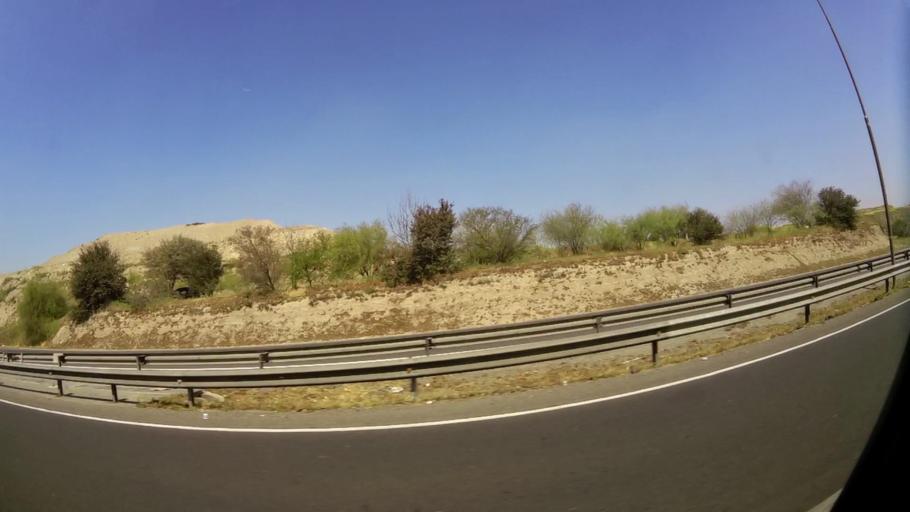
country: CL
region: Santiago Metropolitan
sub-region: Provincia de Santiago
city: Lo Prado
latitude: -33.4829
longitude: -70.7131
